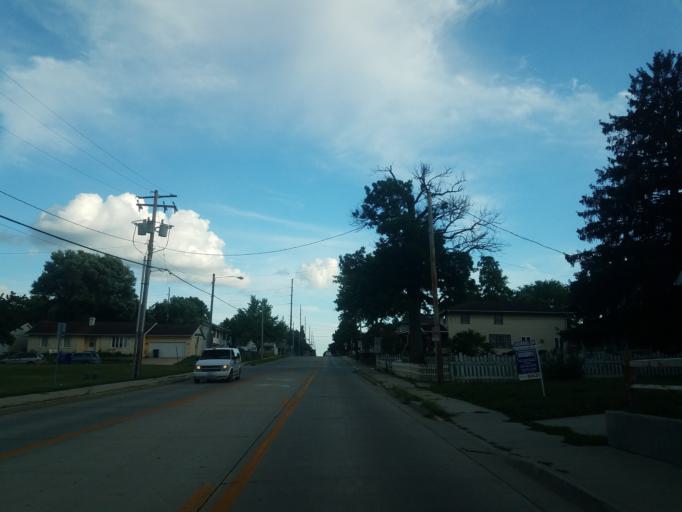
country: US
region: Illinois
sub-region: McLean County
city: Bloomington
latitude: 40.4747
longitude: -89.0065
